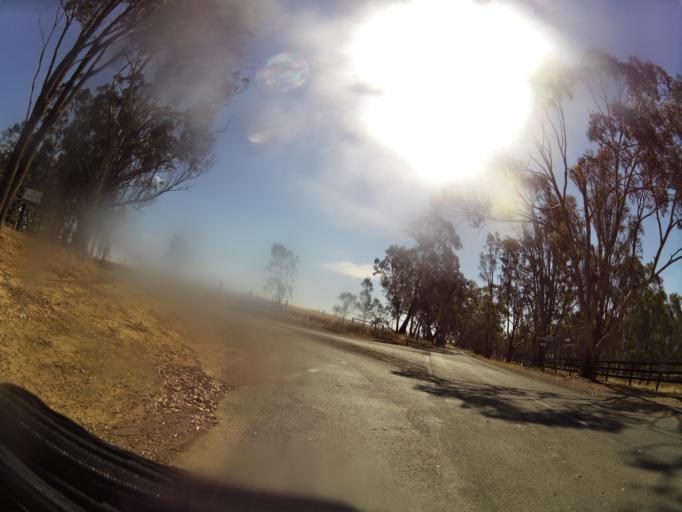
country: AU
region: Victoria
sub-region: Campaspe
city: Kyabram
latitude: -36.8596
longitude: 145.0887
